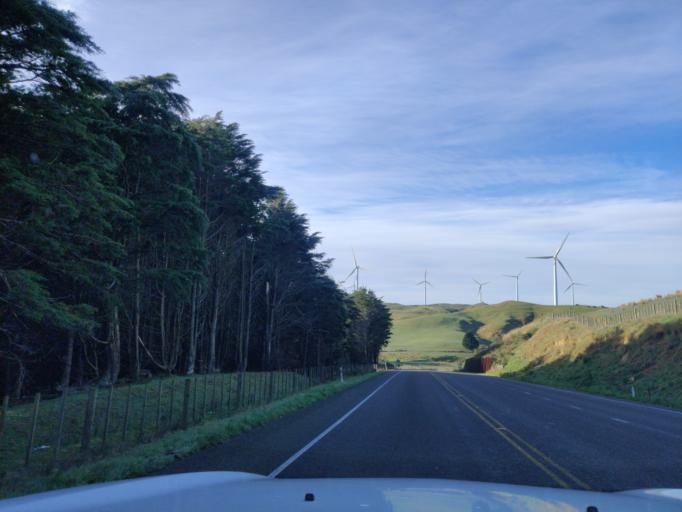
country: NZ
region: Manawatu-Wanganui
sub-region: Palmerston North City
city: Palmerston North
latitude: -40.2975
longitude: 175.8095
